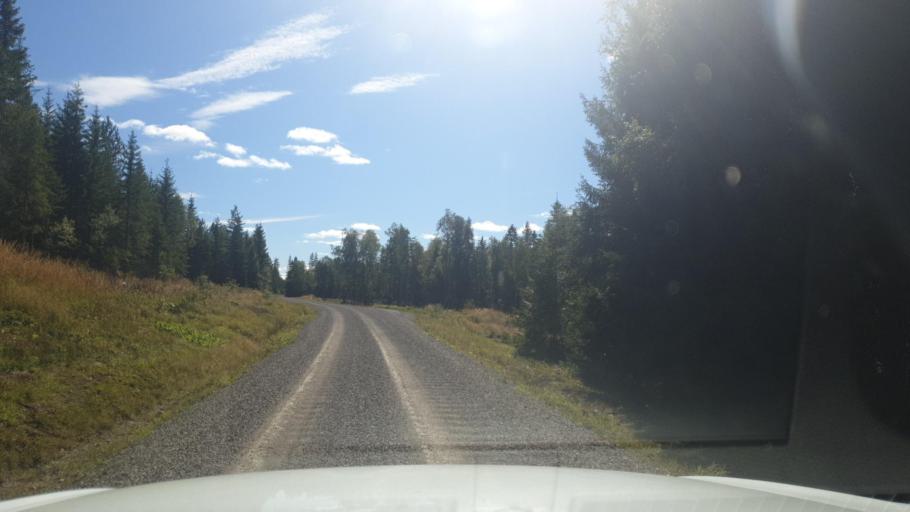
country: SE
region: Vaermland
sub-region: Eda Kommun
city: Charlottenberg
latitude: 60.0790
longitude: 12.6197
